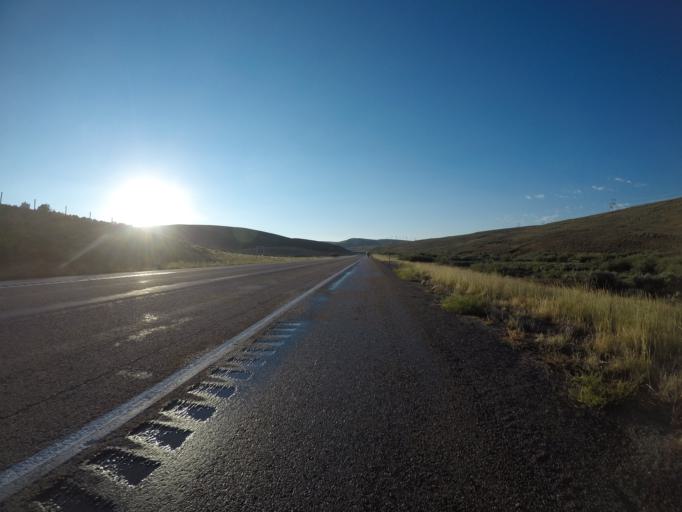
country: US
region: Wyoming
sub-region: Lincoln County
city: Kemmerer
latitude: 41.8710
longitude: -110.5129
